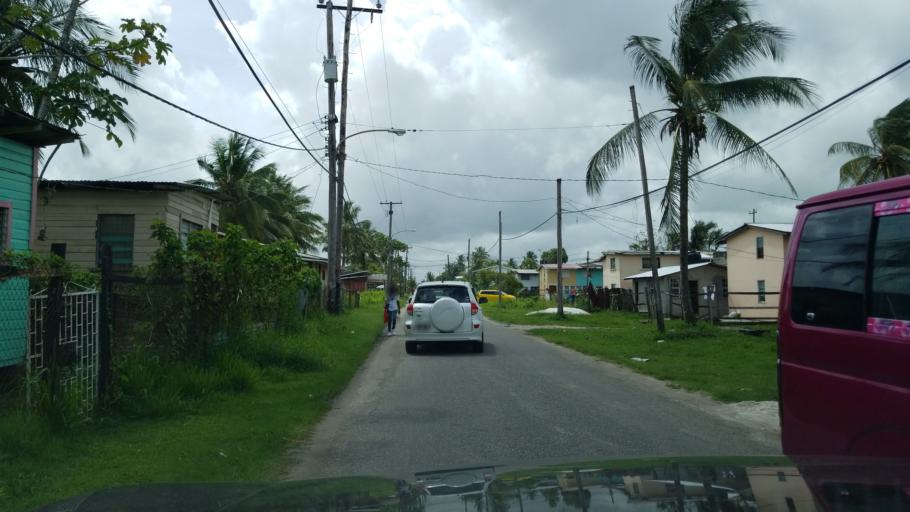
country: GY
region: Demerara-Mahaica
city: Georgetown
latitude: 6.7929
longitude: -58.1519
